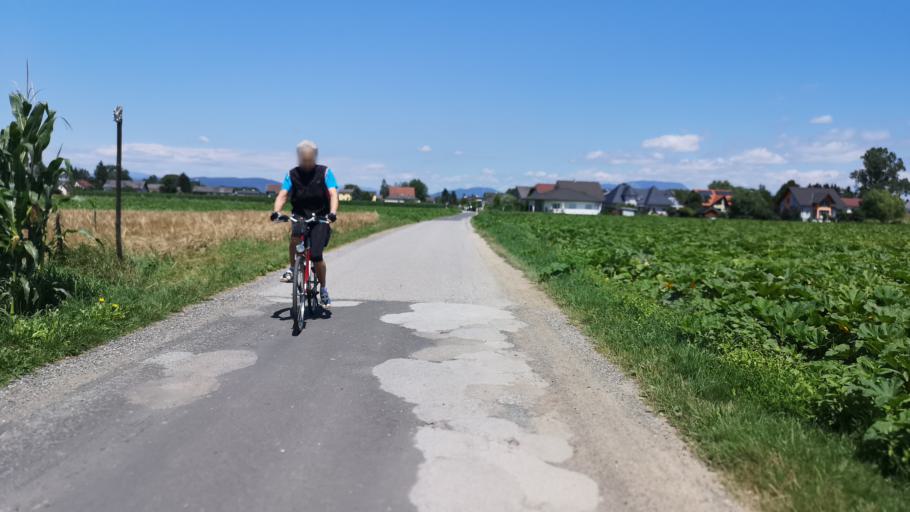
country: AT
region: Styria
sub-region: Politischer Bezirk Graz-Umgebung
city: Gossendorf
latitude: 46.9881
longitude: 15.4881
